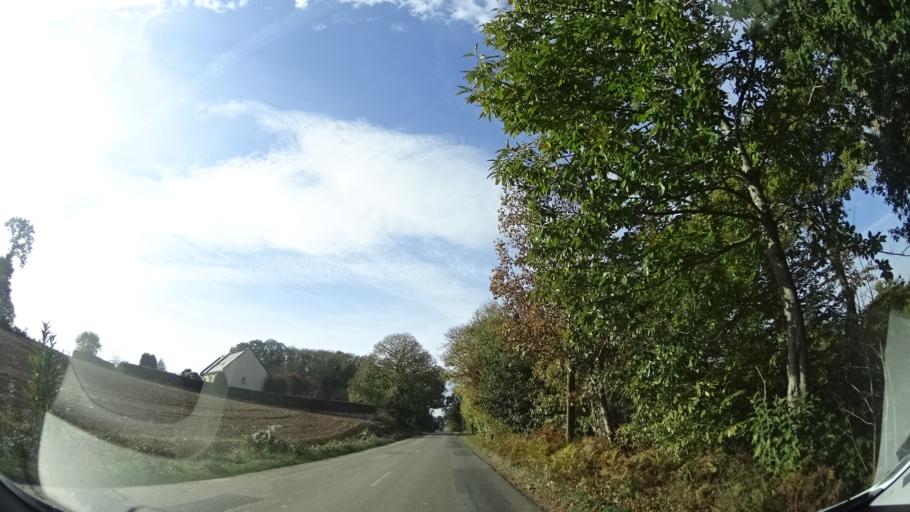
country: FR
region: Brittany
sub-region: Departement d'Ille-et-Vilaine
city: Geveze
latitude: 48.2160
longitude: -1.8319
